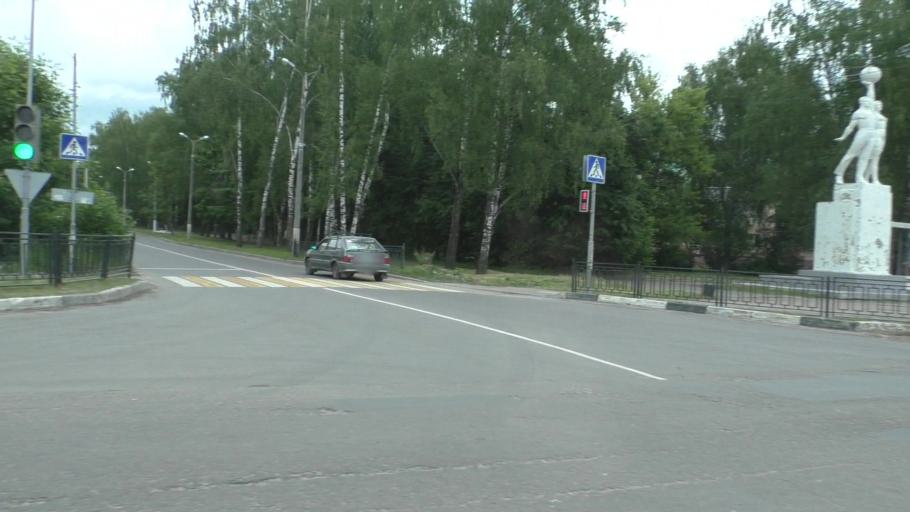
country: RU
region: Moskovskaya
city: Yegor'yevsk
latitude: 55.3725
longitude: 39.0552
